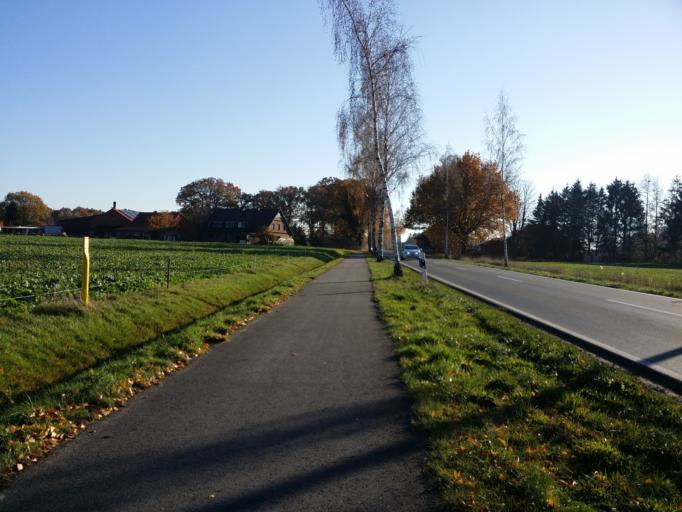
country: DE
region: Lower Saxony
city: Langwedel
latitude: 53.0392
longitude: 9.1533
